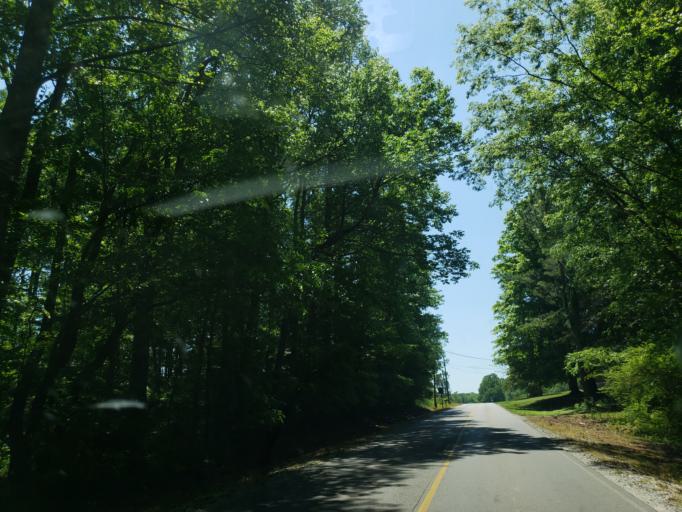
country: US
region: Alabama
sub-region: Madison County
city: Harvest
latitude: 34.9123
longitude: -86.7308
